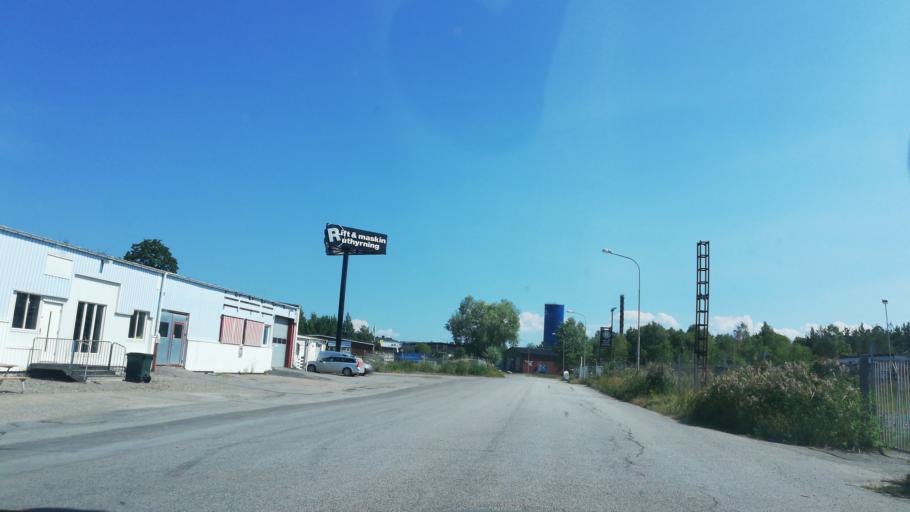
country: SE
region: OEstergoetland
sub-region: Finspangs Kommun
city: Finspang
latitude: 58.7015
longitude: 15.8000
